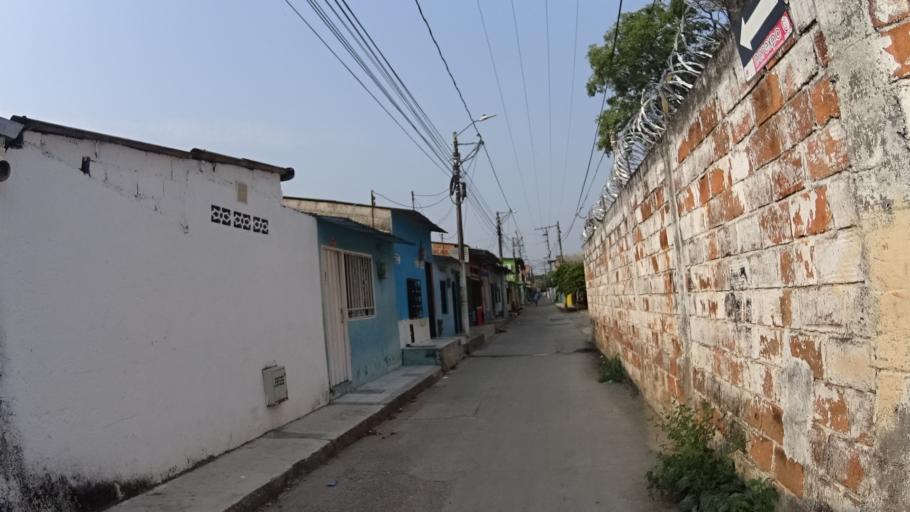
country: CO
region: Cundinamarca
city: Puerto Salgar
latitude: 5.4761
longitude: -74.6784
